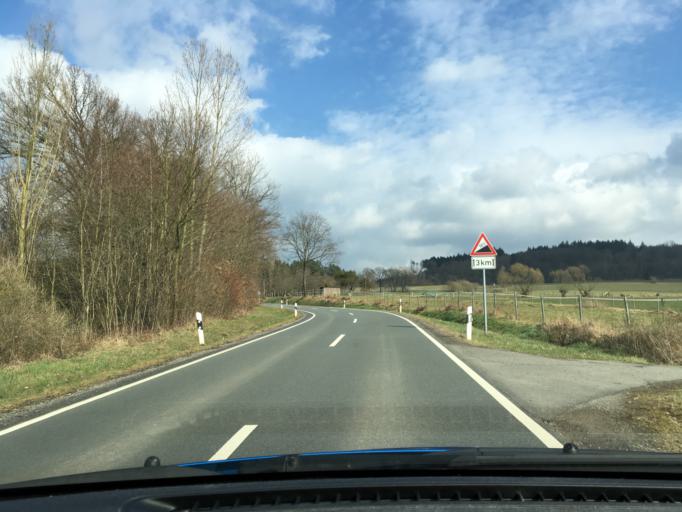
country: DE
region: Lower Saxony
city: Bodenfelde
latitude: 51.5889
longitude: 9.6027
